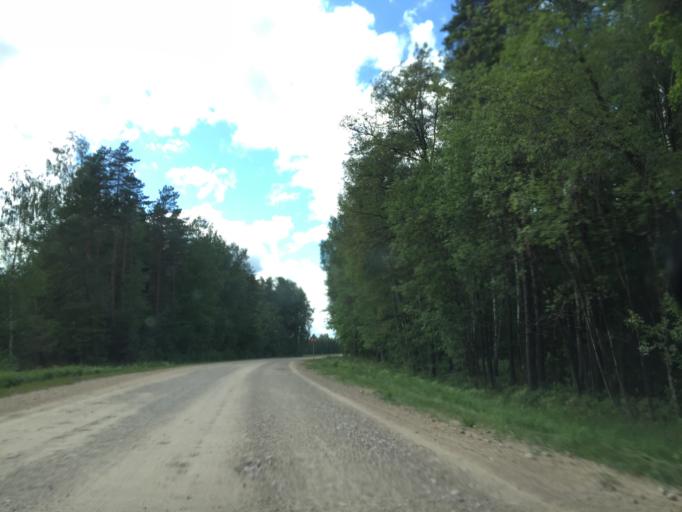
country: LV
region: Vecumnieki
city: Vecumnieki
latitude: 56.4223
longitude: 24.5023
